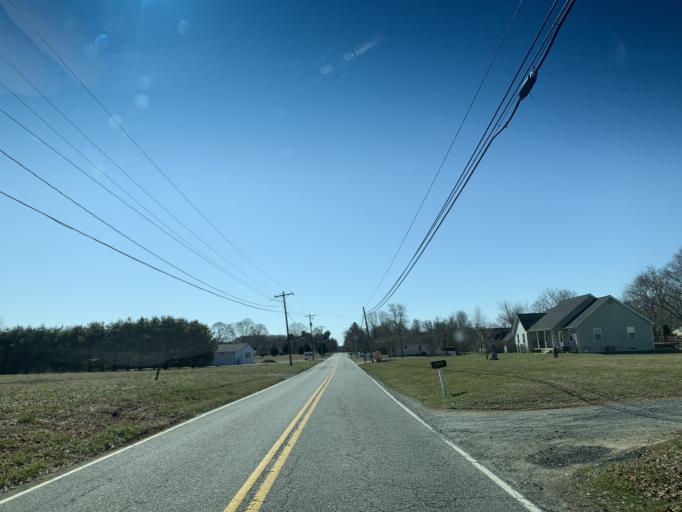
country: US
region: Maryland
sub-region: Cecil County
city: Rising Sun
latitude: 39.6316
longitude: -76.0769
